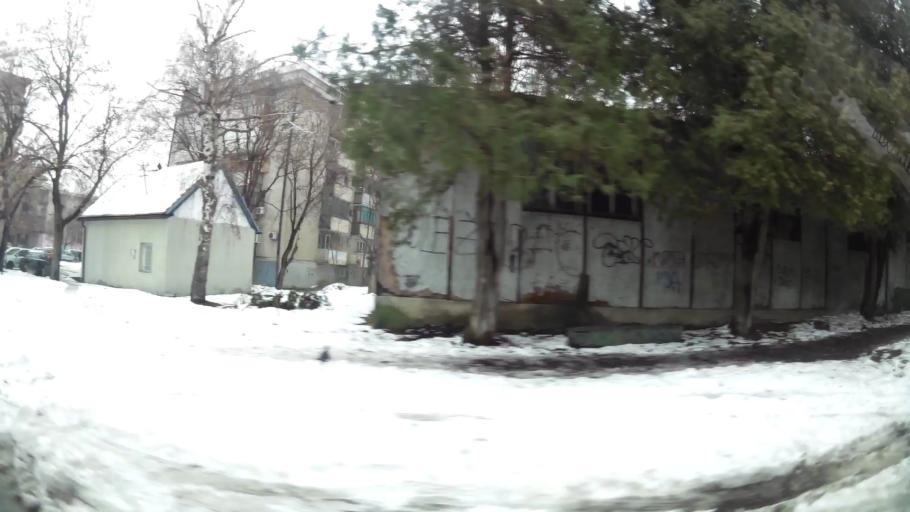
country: RS
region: Central Serbia
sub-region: Belgrade
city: Zemun
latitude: 44.8519
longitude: 20.3908
